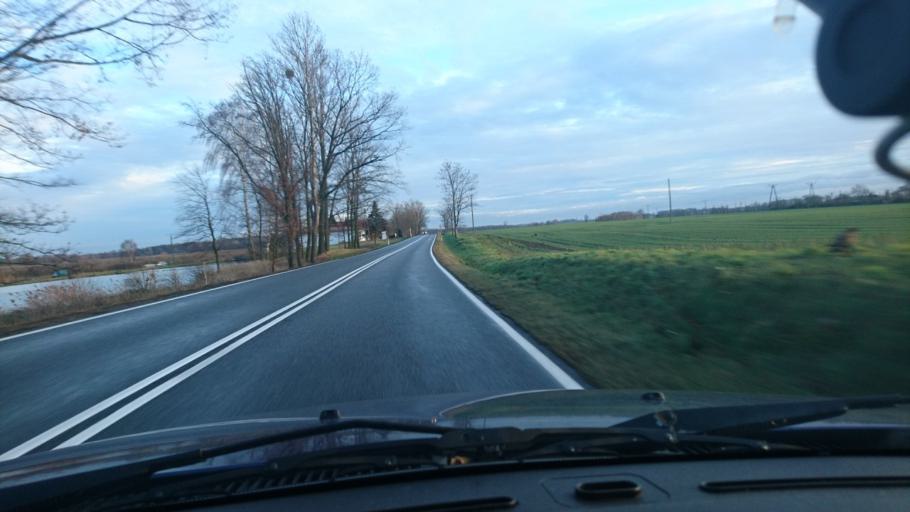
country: PL
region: Lodz Voivodeship
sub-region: Powiat wieruszowski
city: Boleslawiec
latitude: 51.1595
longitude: 18.1644
